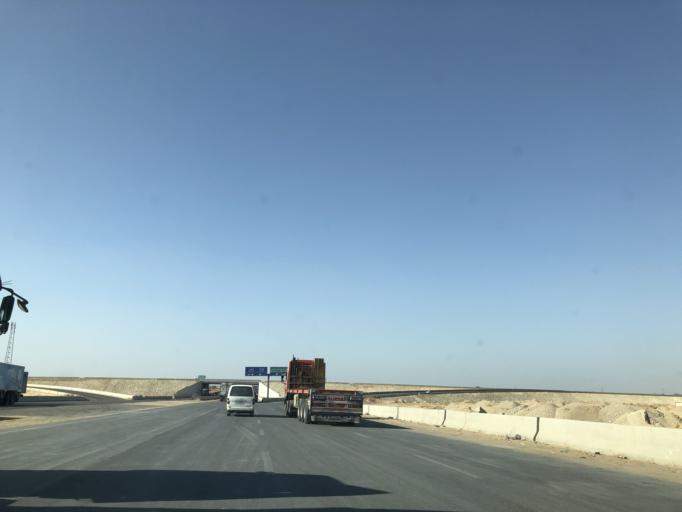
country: EG
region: Muhafazat al Minufiyah
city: Ashmun
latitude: 30.0643
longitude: 30.8459
